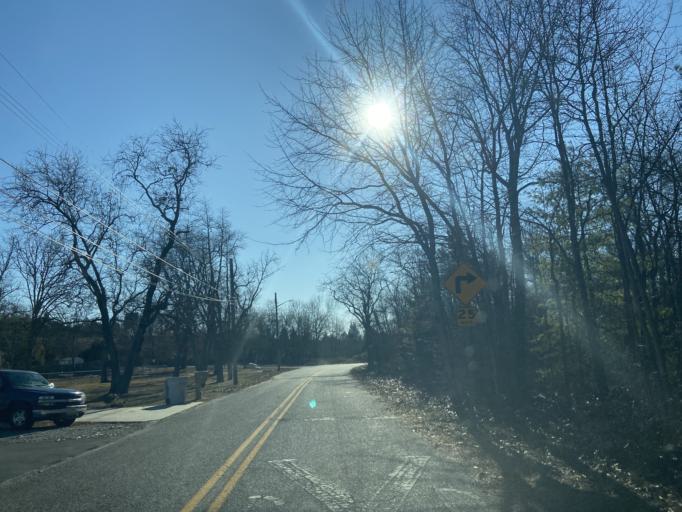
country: US
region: New Jersey
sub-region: Cumberland County
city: Vineland
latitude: 39.4934
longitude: -75.0722
